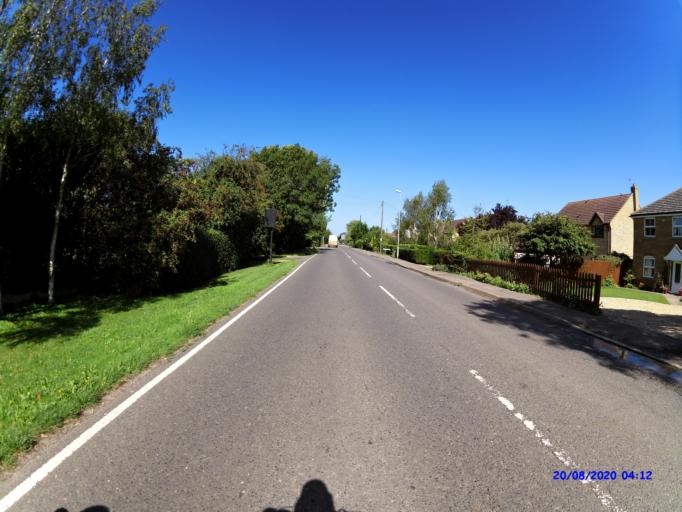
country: GB
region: England
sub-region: Cambridgeshire
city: Ramsey
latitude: 52.4824
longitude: -0.1053
